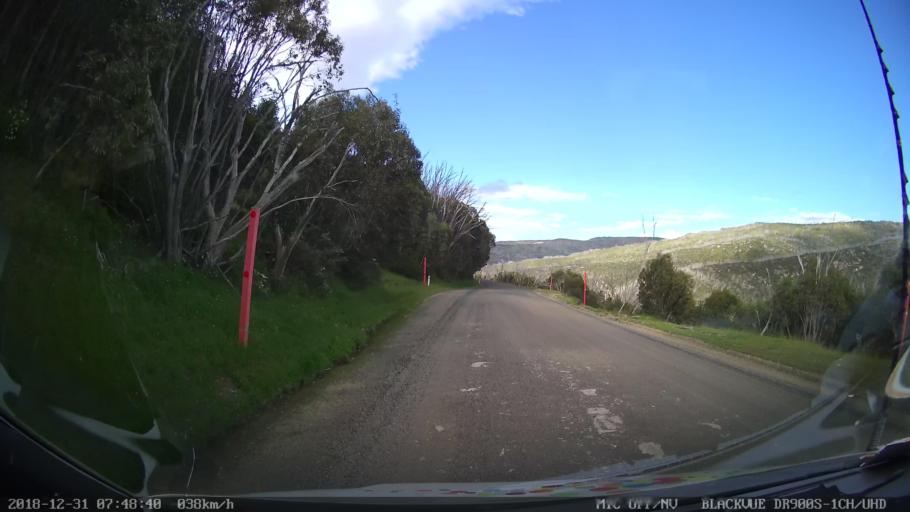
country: AU
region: New South Wales
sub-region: Snowy River
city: Jindabyne
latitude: -36.3691
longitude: 148.3899
